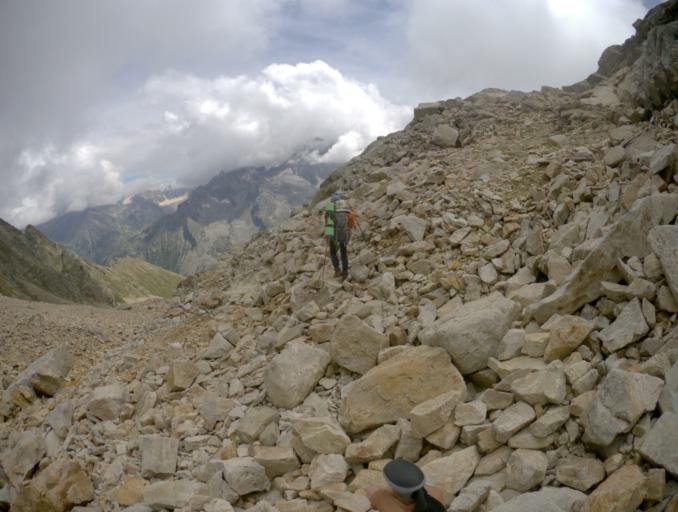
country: RU
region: Karachayevo-Cherkesiya
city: Uchkulan
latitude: 43.2766
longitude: 42.1192
